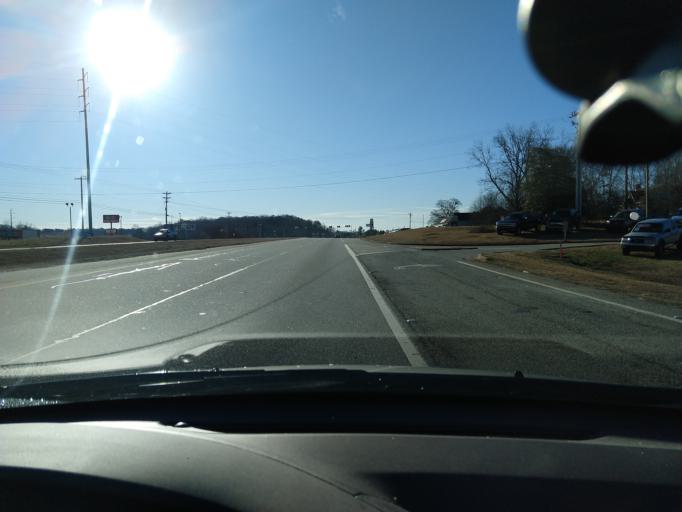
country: US
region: Georgia
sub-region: Jackson County
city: Commerce
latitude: 34.2374
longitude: -83.4547
